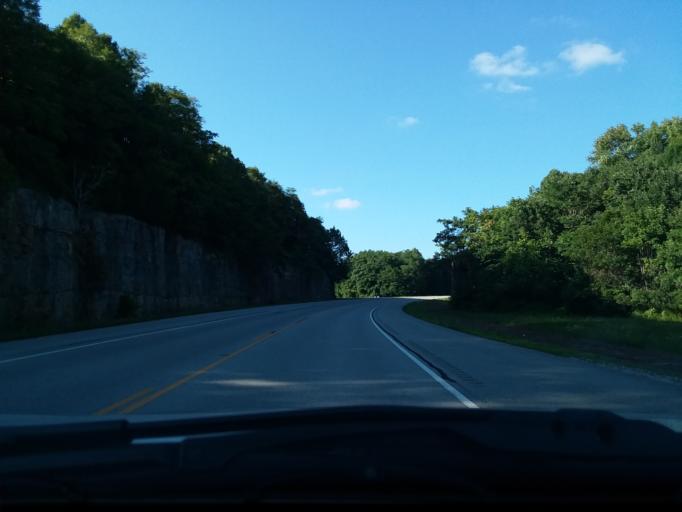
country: US
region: Tennessee
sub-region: Clay County
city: Celina
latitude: 36.5753
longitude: -85.4474
